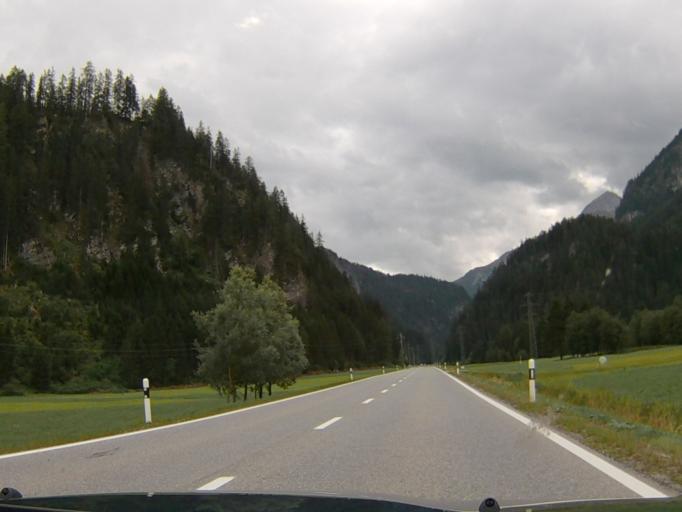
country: CH
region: Grisons
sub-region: Albula District
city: Tiefencastel
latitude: 46.5515
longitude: 9.6250
